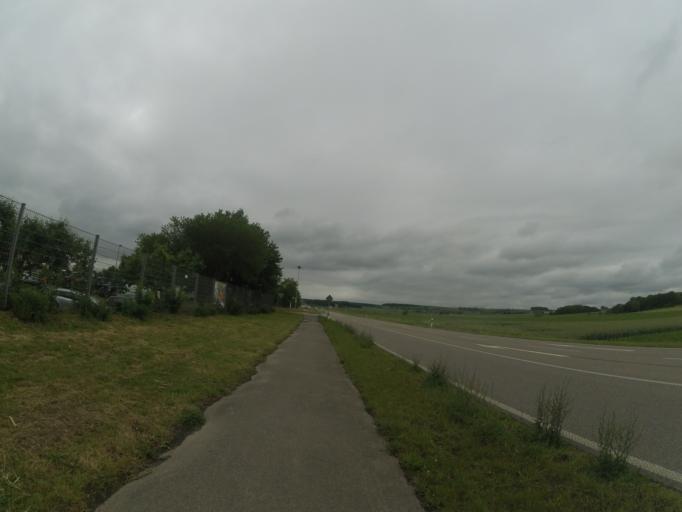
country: DE
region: Baden-Wuerttemberg
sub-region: Tuebingen Region
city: Nerenstetten
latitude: 48.4963
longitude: 10.0795
